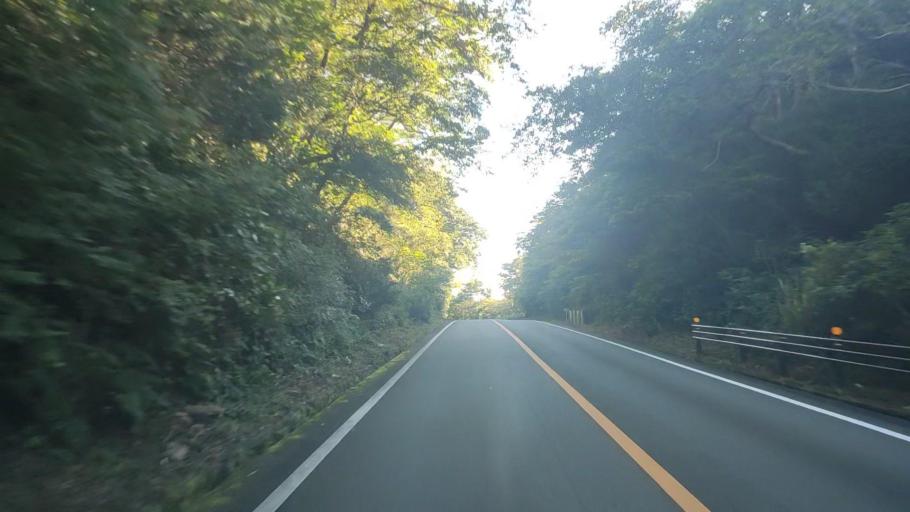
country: JP
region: Mie
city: Toba
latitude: 34.4084
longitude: 136.8915
